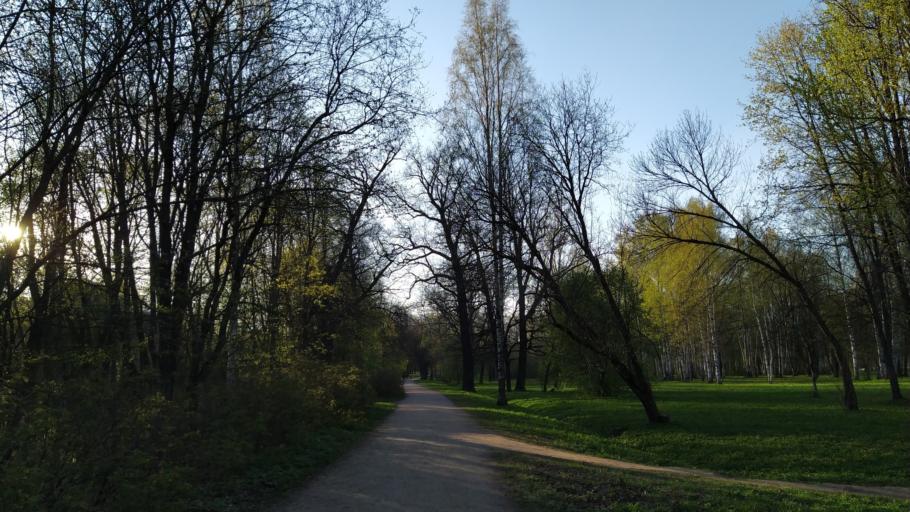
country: RU
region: St.-Petersburg
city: Pavlovsk
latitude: 59.6981
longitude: 30.4284
